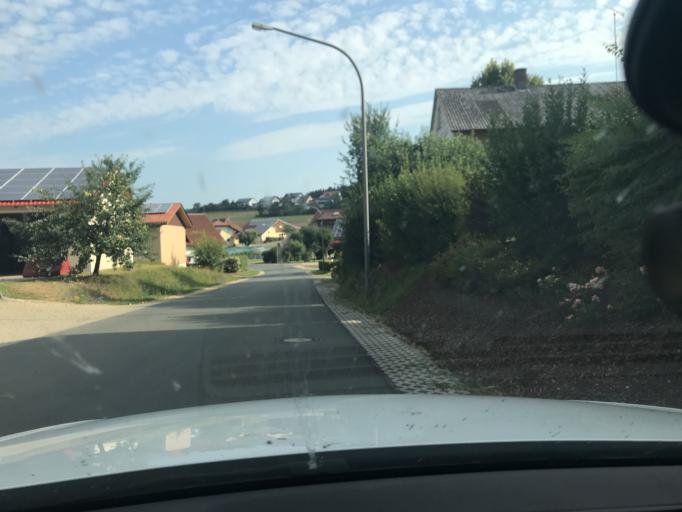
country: DE
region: Bavaria
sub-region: Upper Palatinate
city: Auerbach
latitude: 49.7193
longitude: 11.6185
